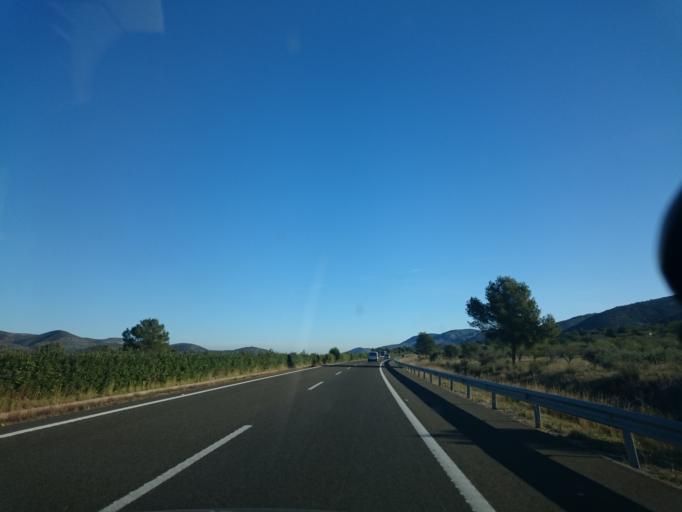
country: ES
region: Valencia
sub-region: Provincia de Castello
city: Santa Magdalena de Pulpis
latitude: 40.3428
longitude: 0.2751
